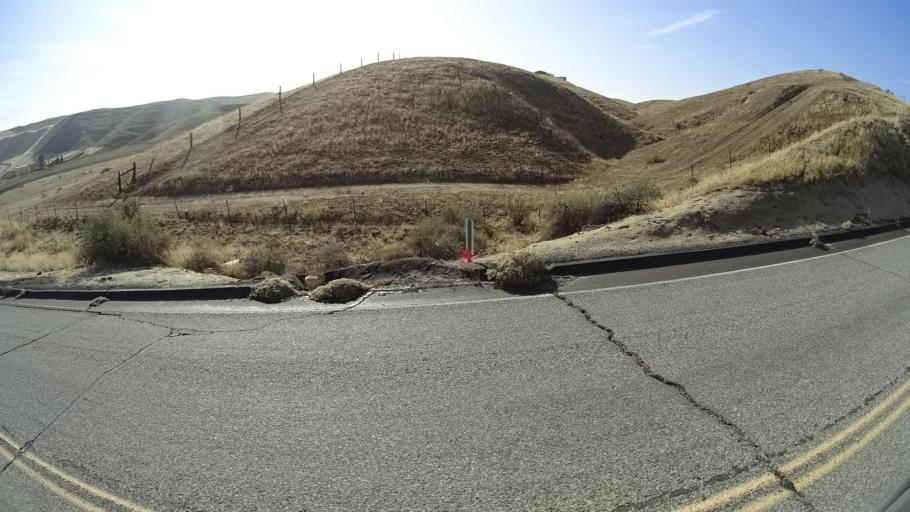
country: US
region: California
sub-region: Kern County
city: Oildale
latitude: 35.5277
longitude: -118.9746
